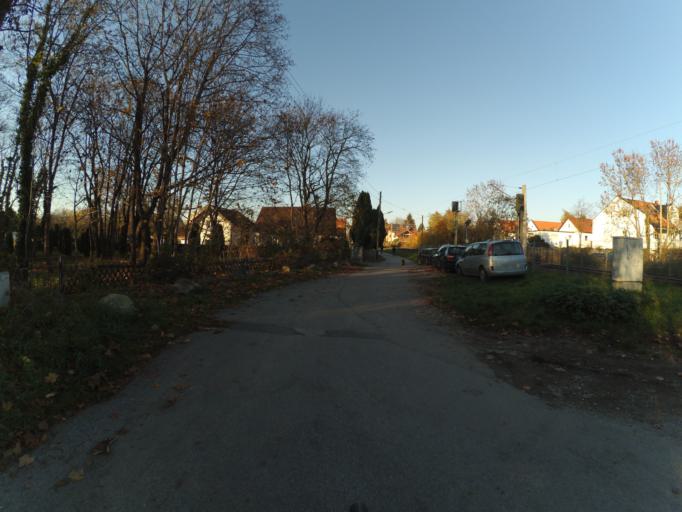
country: DE
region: Bavaria
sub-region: Upper Bavaria
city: Oberschleissheim
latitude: 48.1952
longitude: 11.5414
